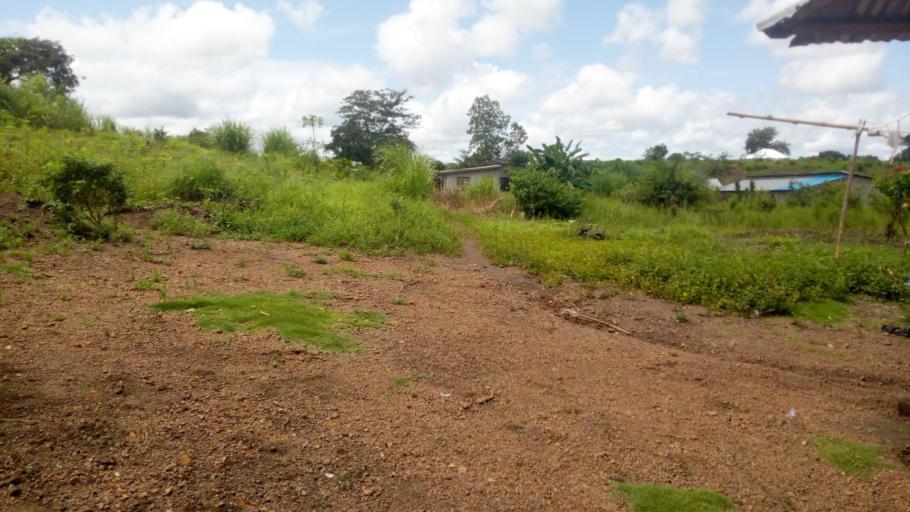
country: SL
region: Northern Province
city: Magburaka
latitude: 8.7121
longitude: -11.9560
